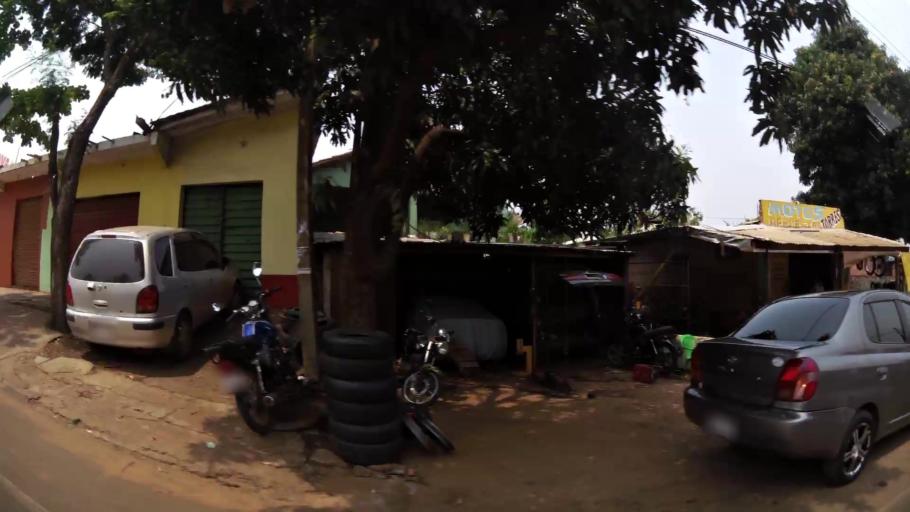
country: BR
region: Parana
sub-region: Foz Do Iguacu
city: Foz do Iguacu
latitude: -25.5655
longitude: -54.6034
